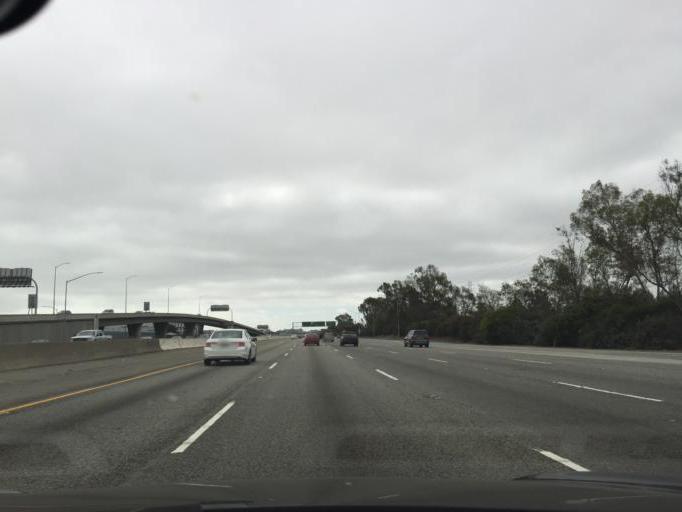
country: US
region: California
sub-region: San Mateo County
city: Millbrae
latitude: 37.6110
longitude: -122.3936
